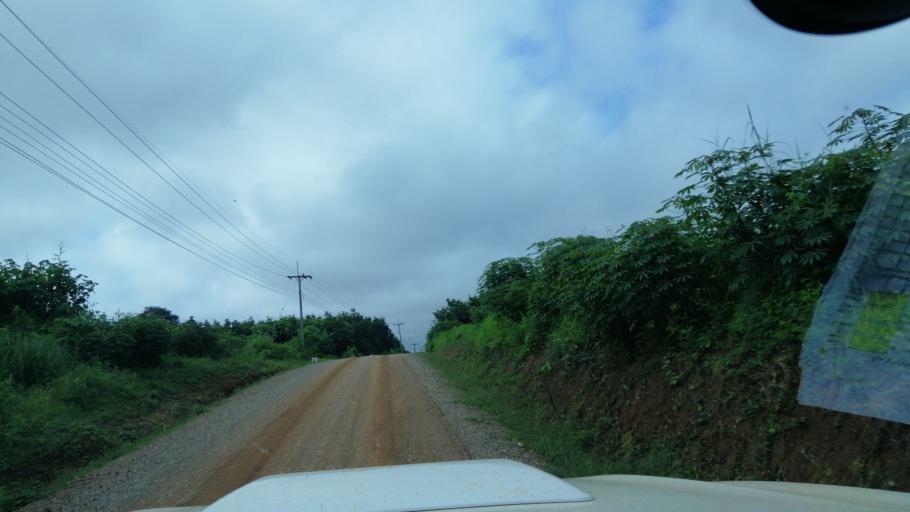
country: LA
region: Xiagnabouli
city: Muang Kenthao
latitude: 17.9860
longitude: 101.4171
